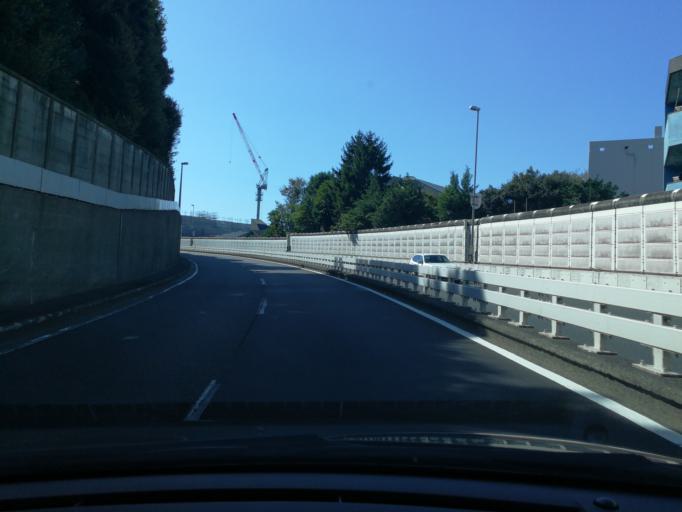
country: JP
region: Tokyo
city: Tokyo
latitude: 35.6406
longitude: 139.7176
